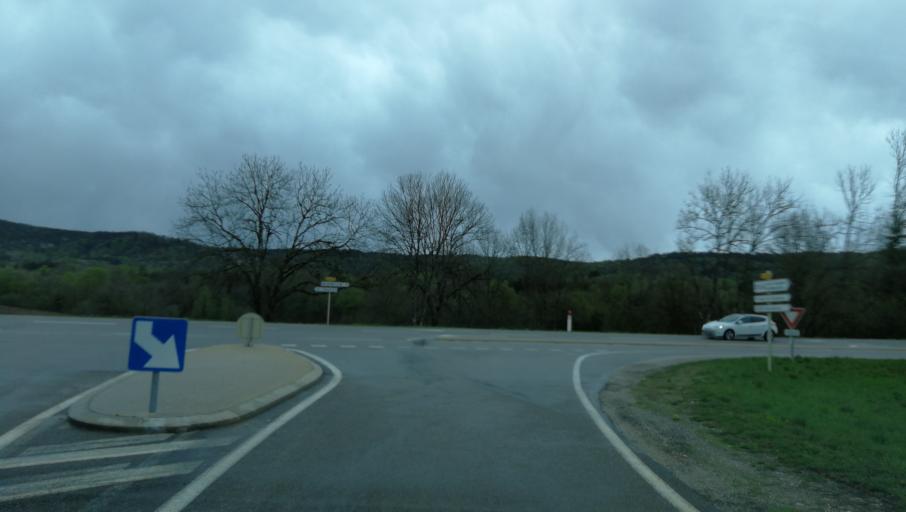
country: FR
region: Franche-Comte
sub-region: Departement du Jura
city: Moirans-en-Montagne
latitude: 46.4571
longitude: 5.7144
